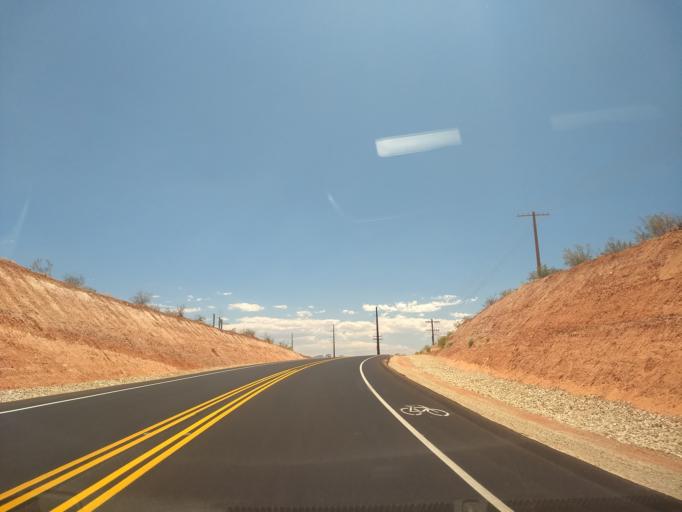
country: US
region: Utah
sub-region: Washington County
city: Washington
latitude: 37.1527
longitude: -113.5177
